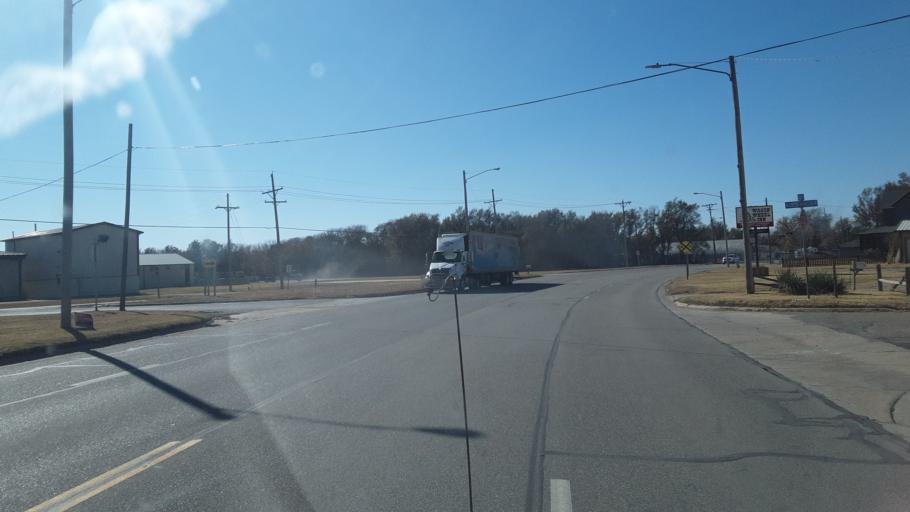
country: US
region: Kansas
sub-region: Rice County
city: Lyons
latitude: 38.3482
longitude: -98.1904
